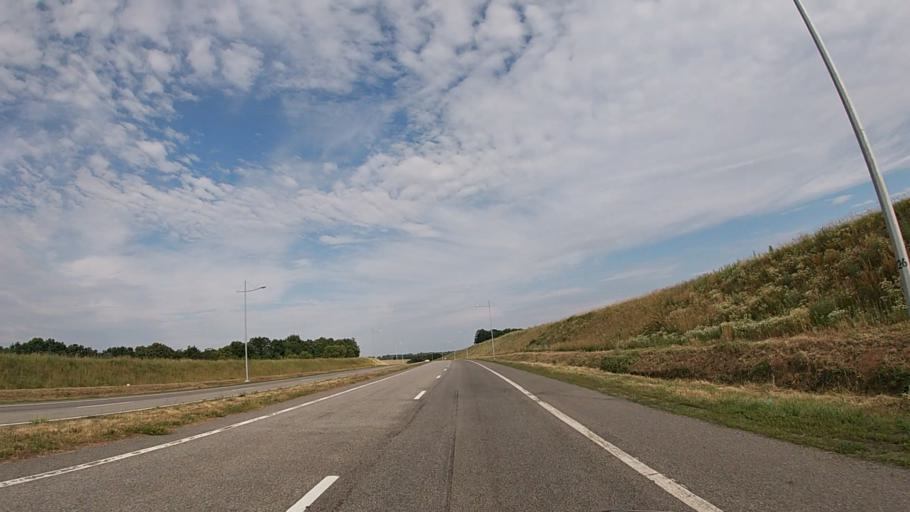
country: RU
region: Belgorod
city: Tomarovka
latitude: 50.7057
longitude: 36.2160
